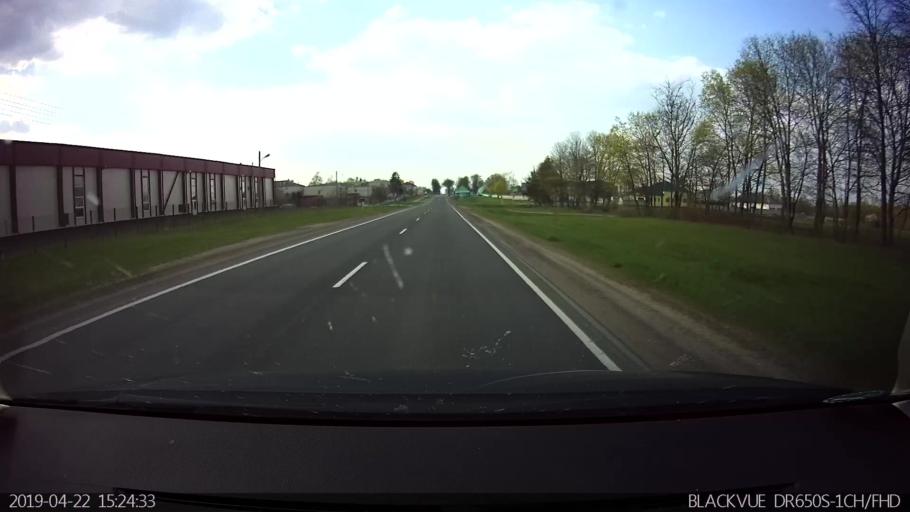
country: BY
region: Brest
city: Vysokaye
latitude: 52.3613
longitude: 23.4064
